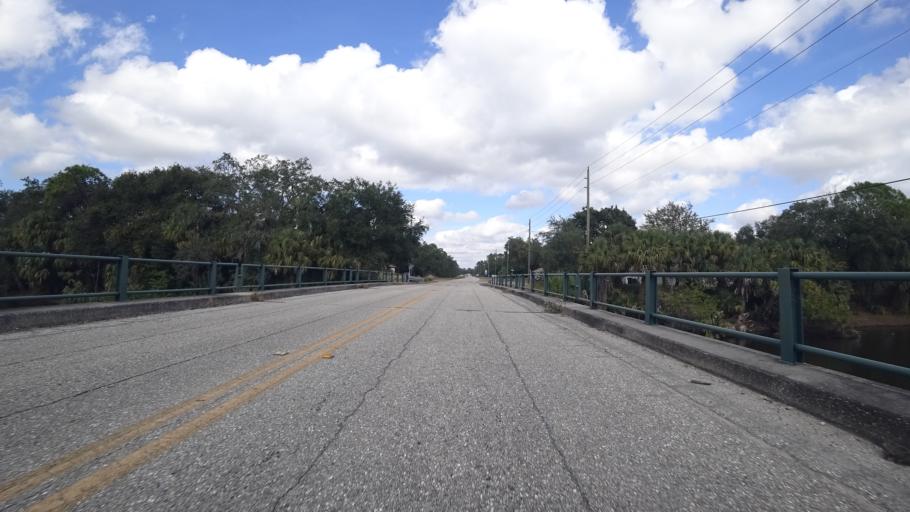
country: US
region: Florida
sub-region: Charlotte County
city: Port Charlotte
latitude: 27.0331
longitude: -82.1337
